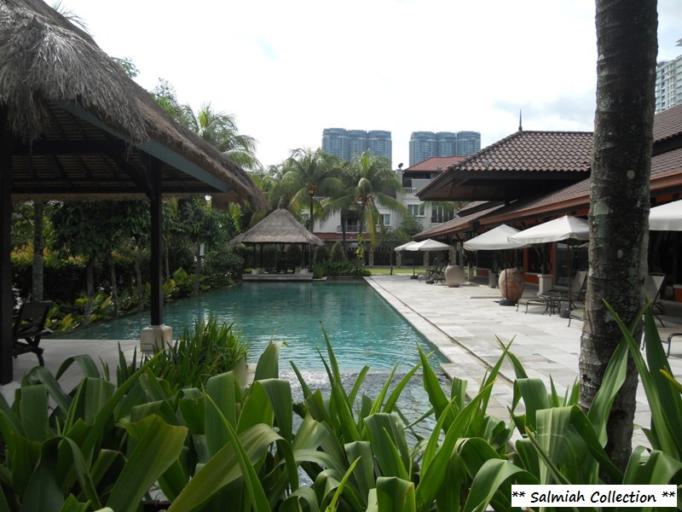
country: MY
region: Kuala Lumpur
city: Kuala Lumpur
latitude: 3.1679
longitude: 101.6658
